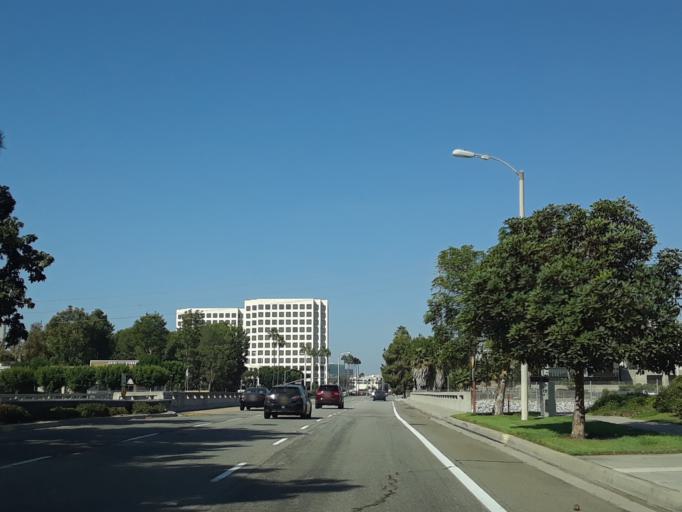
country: US
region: California
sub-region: Orange County
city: Irvine
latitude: 33.6788
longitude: -117.8343
